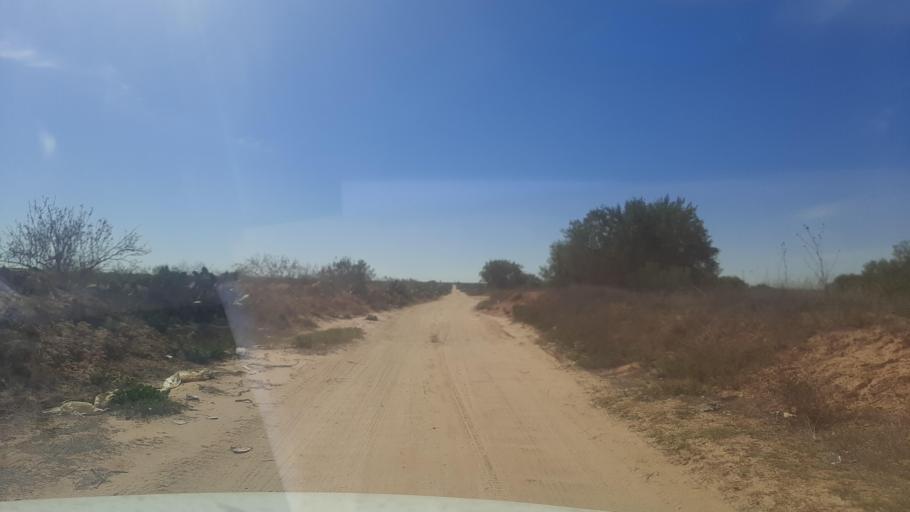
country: TN
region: Safaqis
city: Sfax
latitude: 34.8442
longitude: 10.5606
